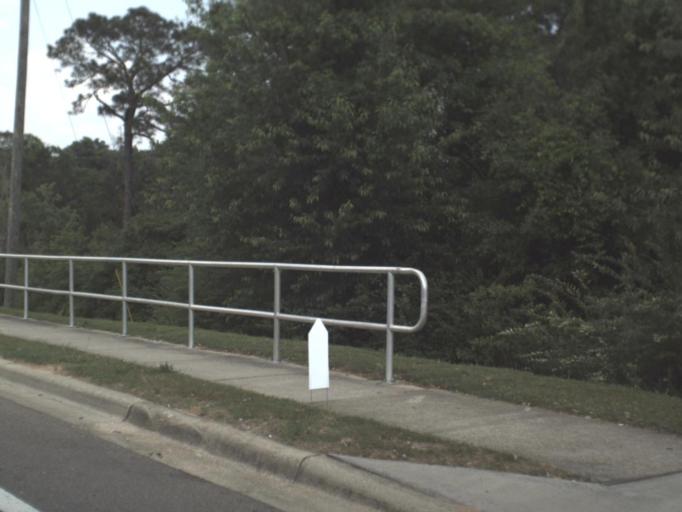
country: US
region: Florida
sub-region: Santa Rosa County
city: Milton
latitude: 30.6273
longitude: -87.0559
